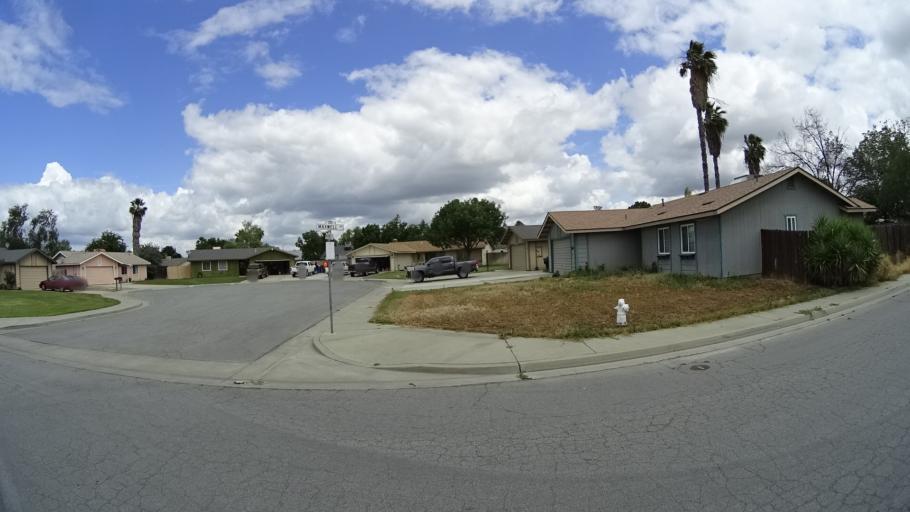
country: US
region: California
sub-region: Kings County
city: Hanford
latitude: 36.3402
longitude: -119.6244
